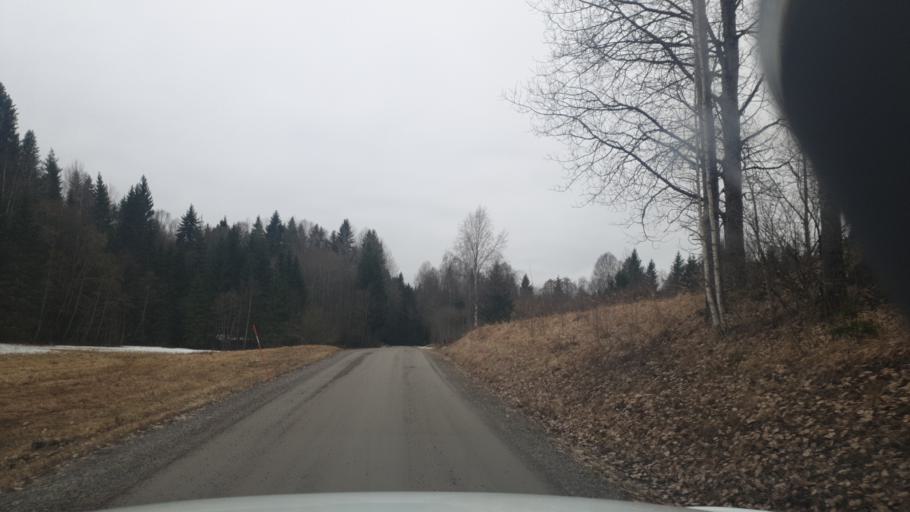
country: NO
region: Ostfold
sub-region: Romskog
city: Romskog
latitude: 59.7035
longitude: 11.9553
